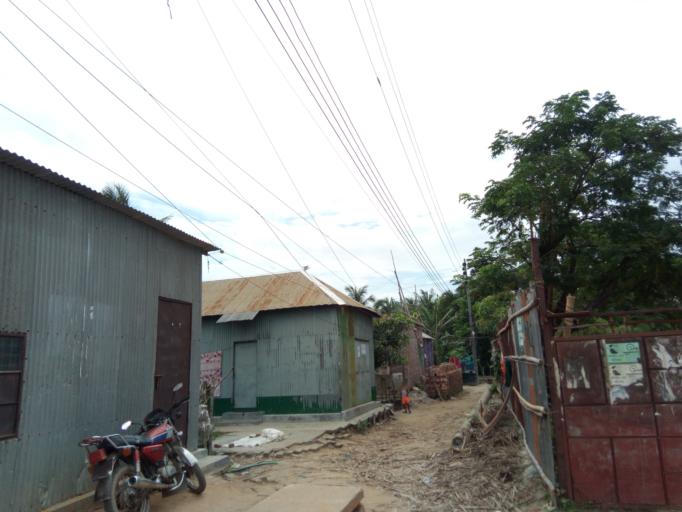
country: BD
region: Dhaka
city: Paltan
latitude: 23.7605
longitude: 90.4641
